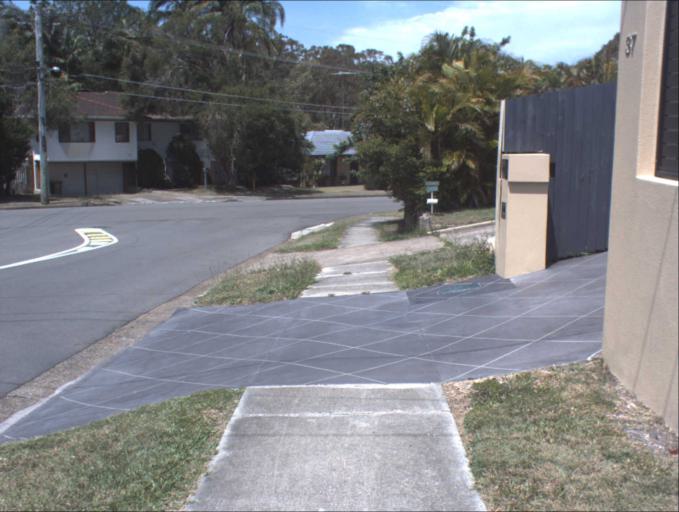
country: AU
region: Queensland
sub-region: Logan
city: Rochedale South
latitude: -27.5953
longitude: 153.1443
